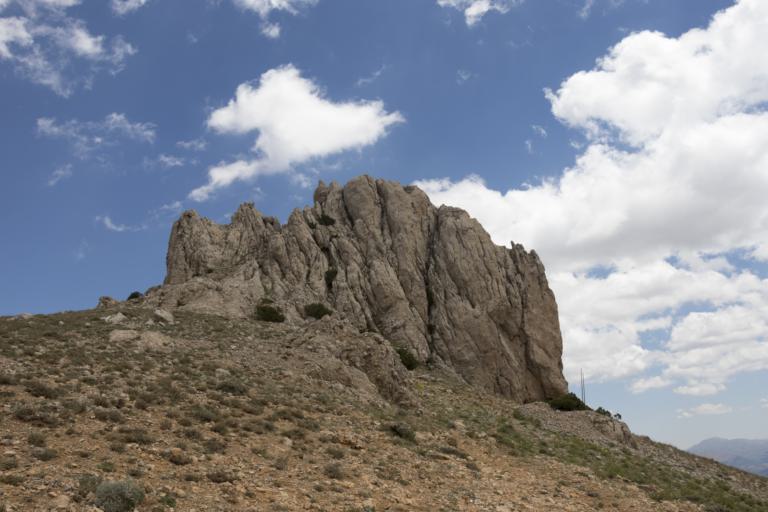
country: TR
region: Adana
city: Tufanbeyli
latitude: 38.3133
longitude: 36.0975
